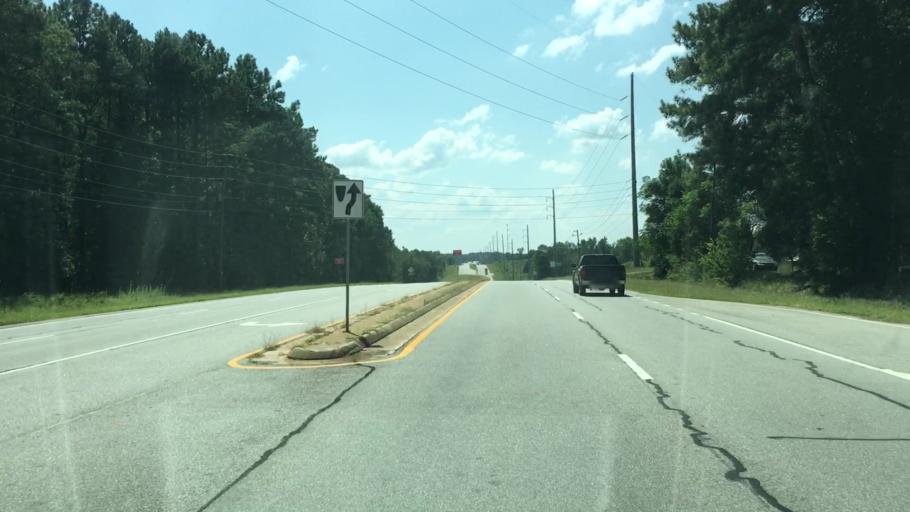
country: US
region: Georgia
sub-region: Morgan County
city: Madison
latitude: 33.5724
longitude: -83.4613
